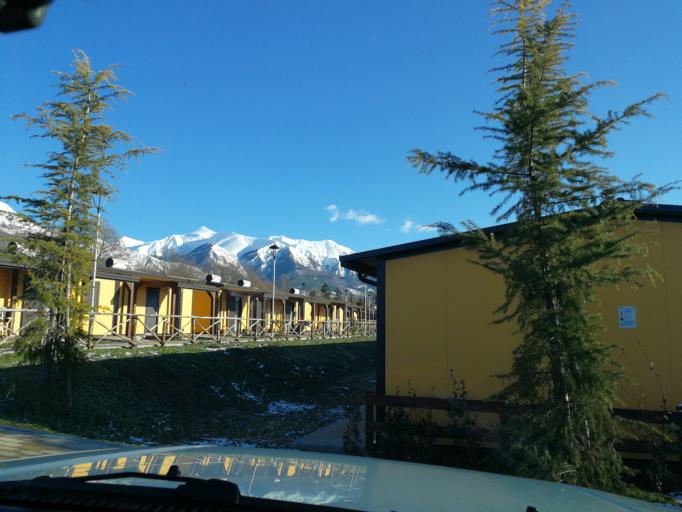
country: IT
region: Latium
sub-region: Provincia di Rieti
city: Amatrice
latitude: 42.6439
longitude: 13.3034
